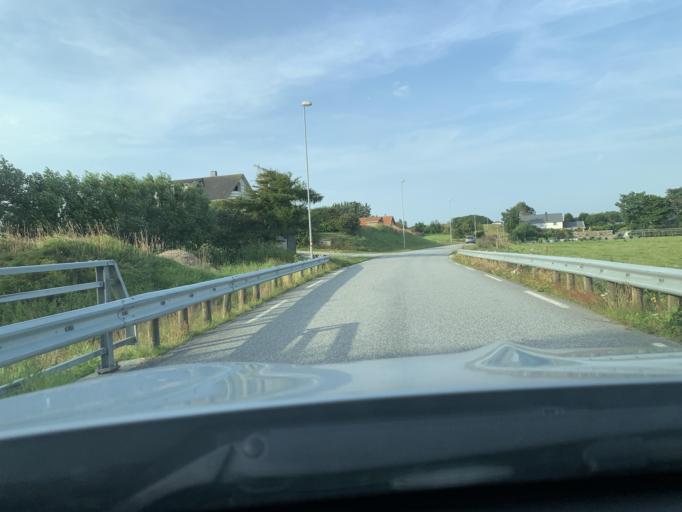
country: NO
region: Rogaland
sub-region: Time
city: Bryne
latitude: 58.7345
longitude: 5.6004
